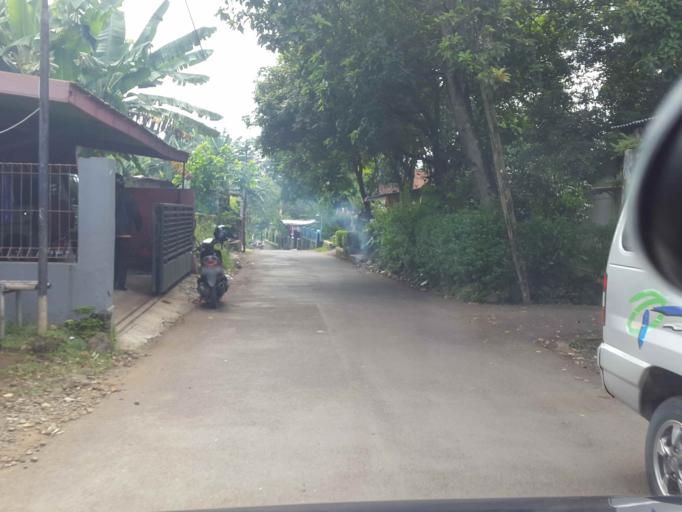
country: ID
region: Central Java
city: Purwokerto
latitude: -7.4096
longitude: 109.2021
